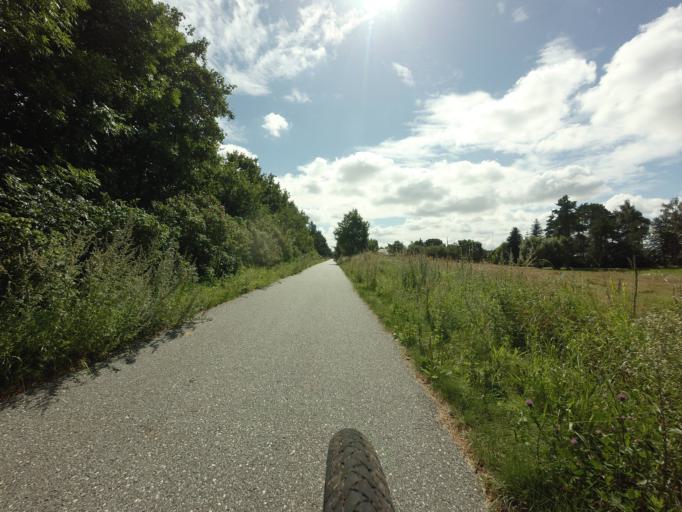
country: DK
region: Central Jutland
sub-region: Norddjurs Kommune
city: Auning
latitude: 56.4356
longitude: 10.3724
